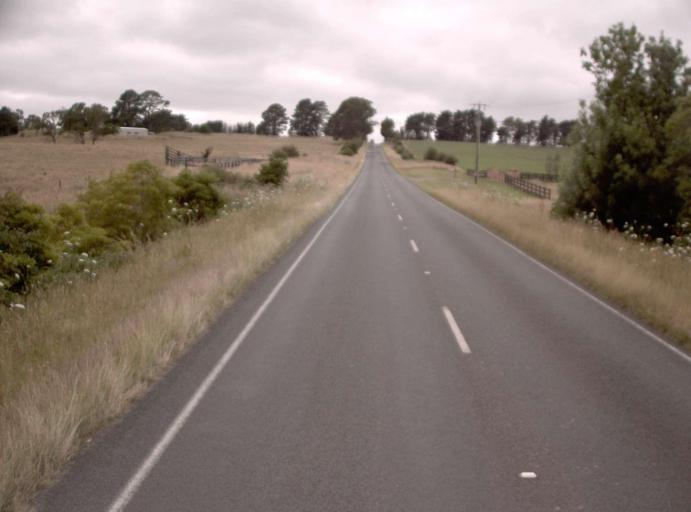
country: AU
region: Victoria
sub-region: Cardinia
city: Bunyip
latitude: -38.1089
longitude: 145.7998
